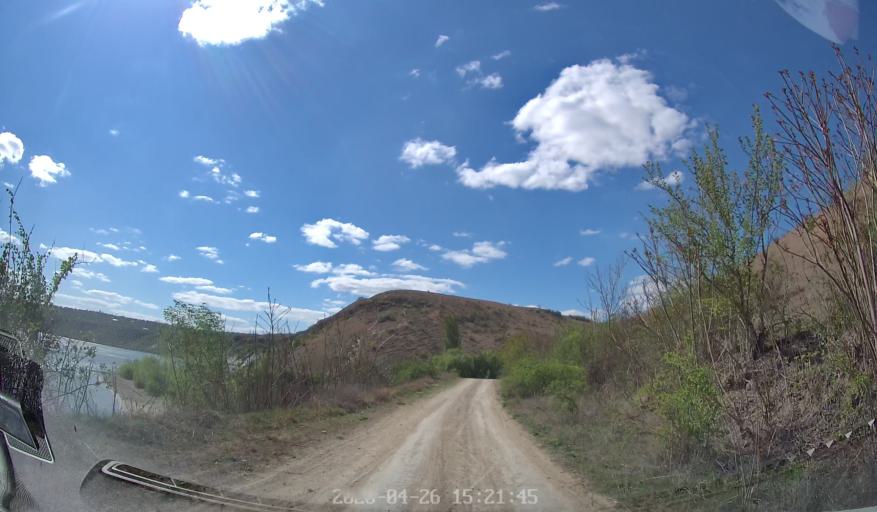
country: MD
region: Telenesti
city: Cocieri
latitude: 47.3646
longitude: 29.0922
